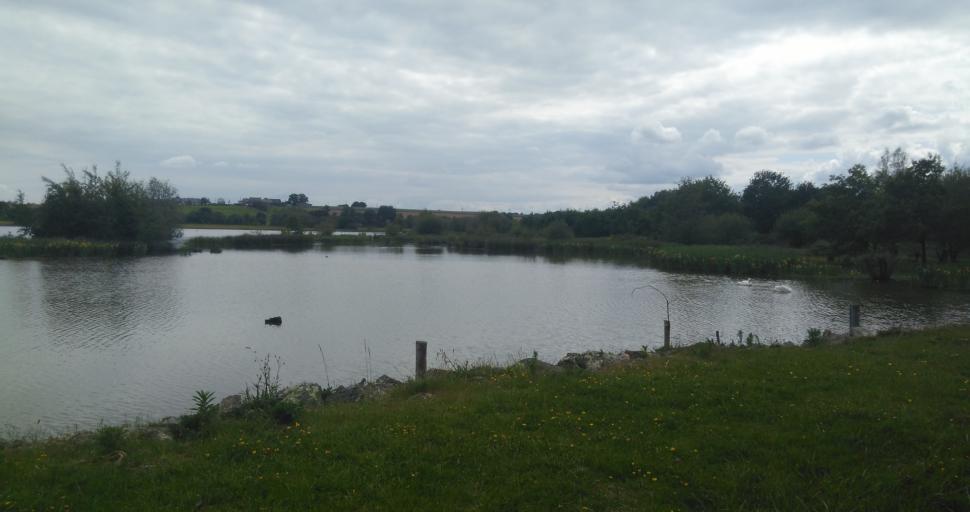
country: FR
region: Brittany
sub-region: Departement d'Ille-et-Vilaine
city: Monterfil
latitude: 48.0752
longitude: -2.0137
